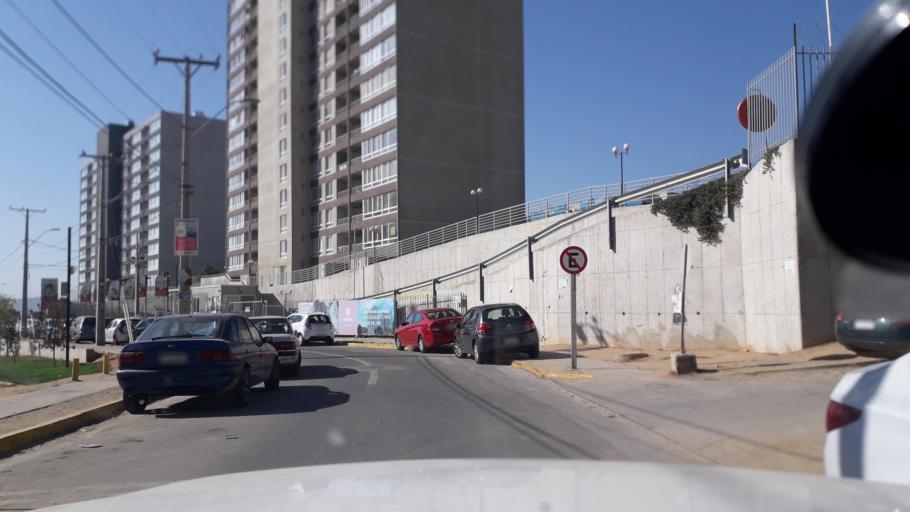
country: CL
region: Valparaiso
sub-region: Provincia de Marga Marga
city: Quilpue
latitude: -33.0686
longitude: -71.4128
